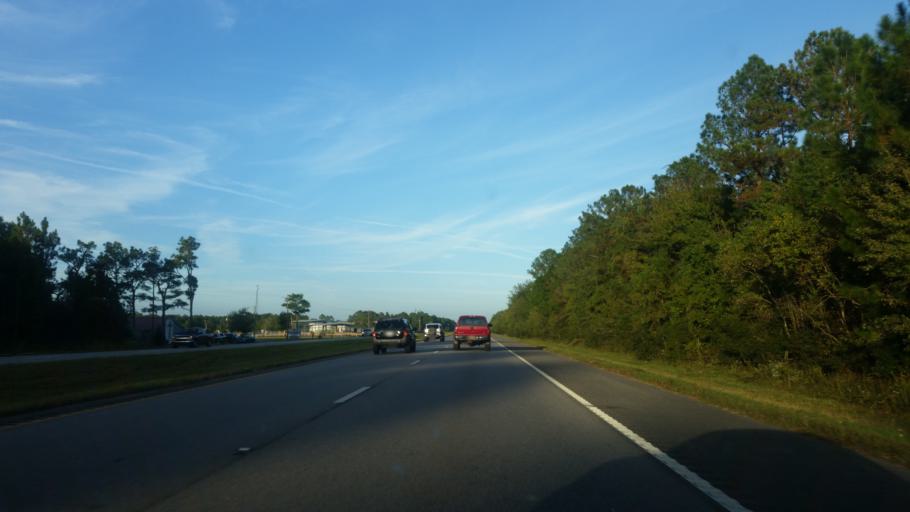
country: US
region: Mississippi
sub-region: Jackson County
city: Moss Point
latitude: 30.4077
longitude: -88.4800
